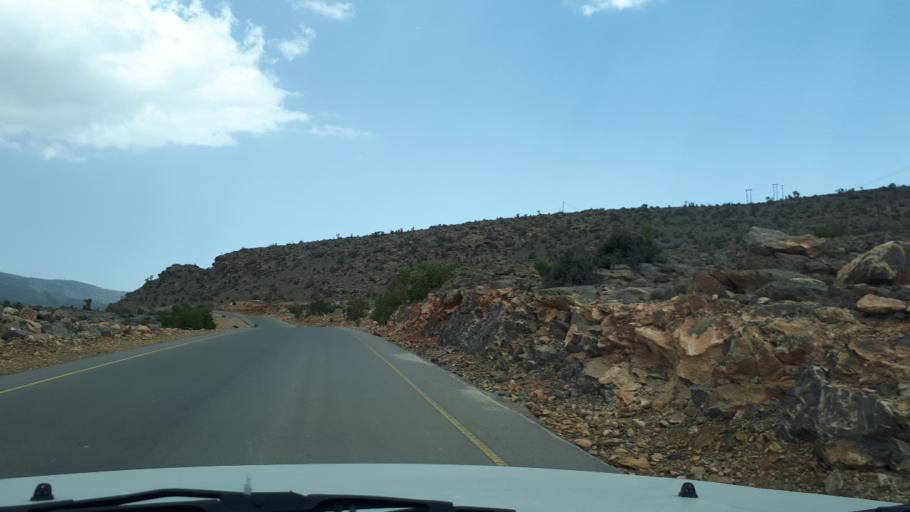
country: OM
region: Muhafazat ad Dakhiliyah
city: Bahla'
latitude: 23.2262
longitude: 57.2014
